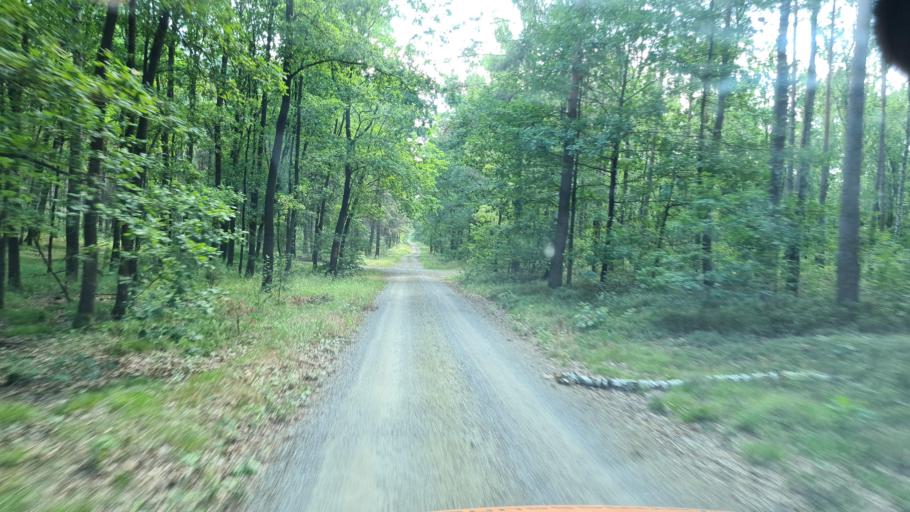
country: DE
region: Brandenburg
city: Hohenbucko
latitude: 51.8001
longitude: 13.5597
